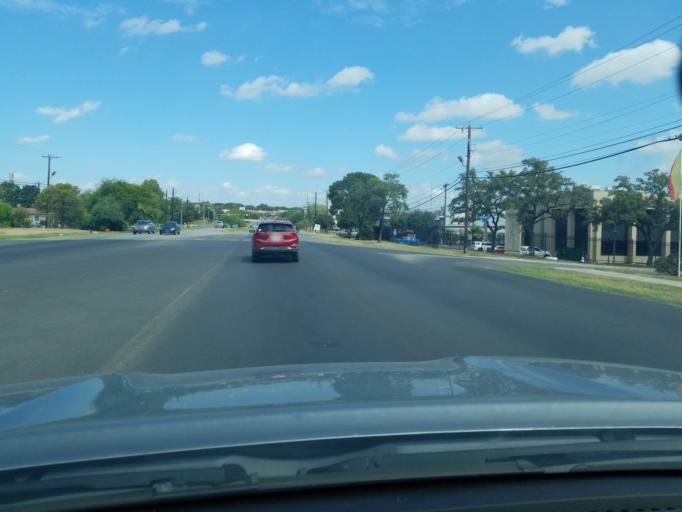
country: US
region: Texas
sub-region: Bexar County
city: Terrell Hills
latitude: 29.4902
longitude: -98.4311
